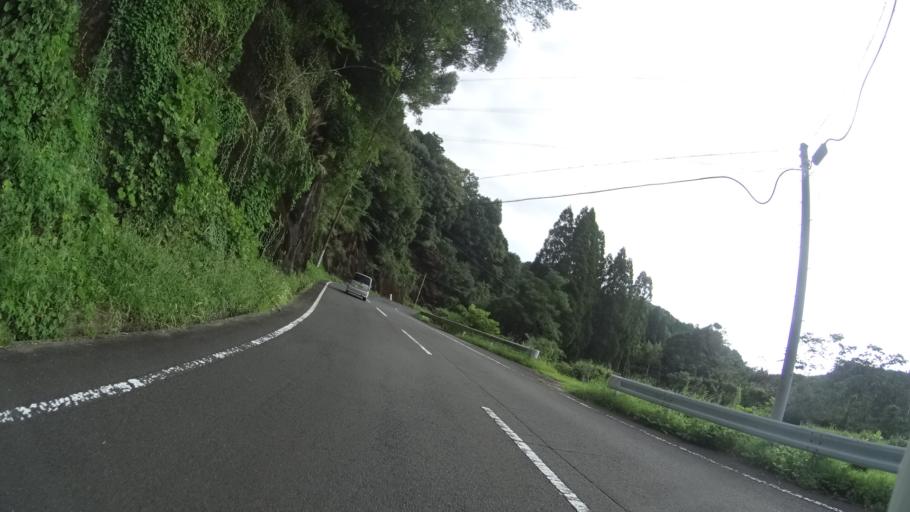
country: JP
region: Kagoshima
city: Okuchi-shinohara
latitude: 32.0241
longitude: 130.6731
